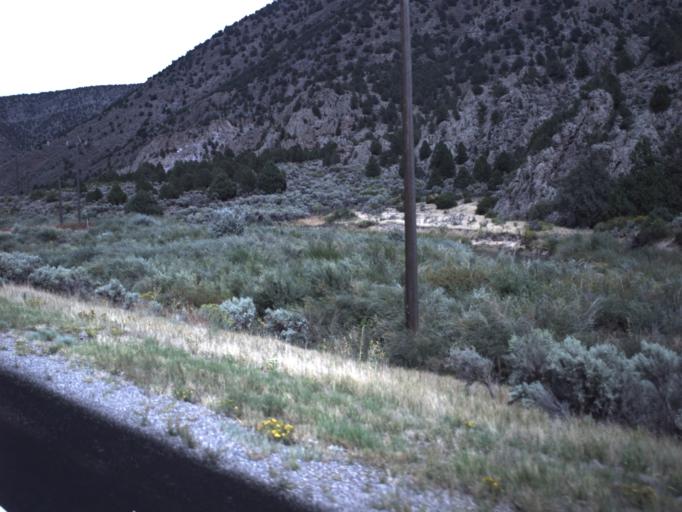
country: US
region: Utah
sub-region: Piute County
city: Junction
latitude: 38.0846
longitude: -112.3401
